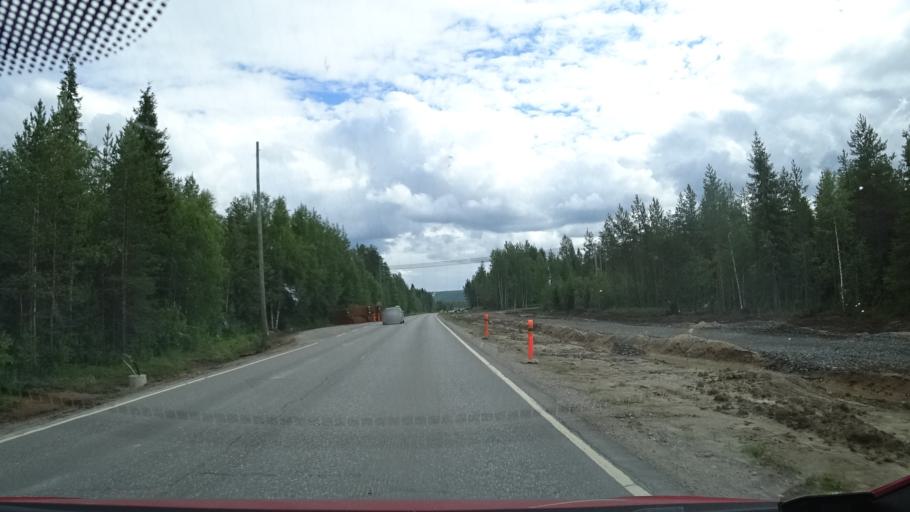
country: FI
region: Lapland
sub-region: Rovaniemi
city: Rovaniemi
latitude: 66.5344
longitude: 25.7309
